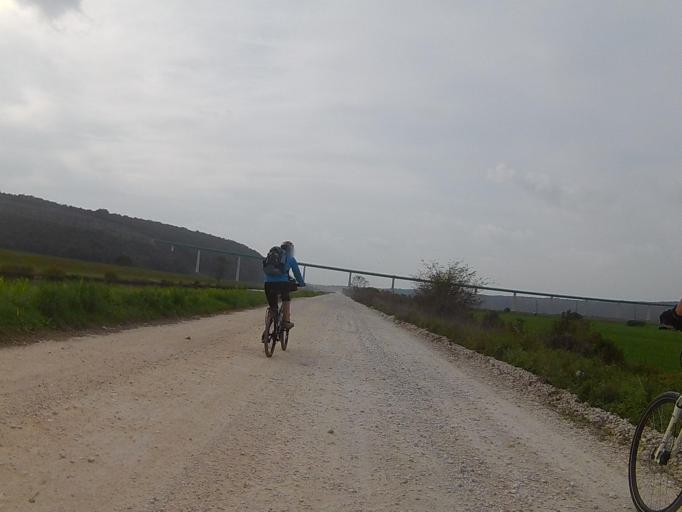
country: HR
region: Istarska
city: Novigrad
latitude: 45.3317
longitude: 13.6368
